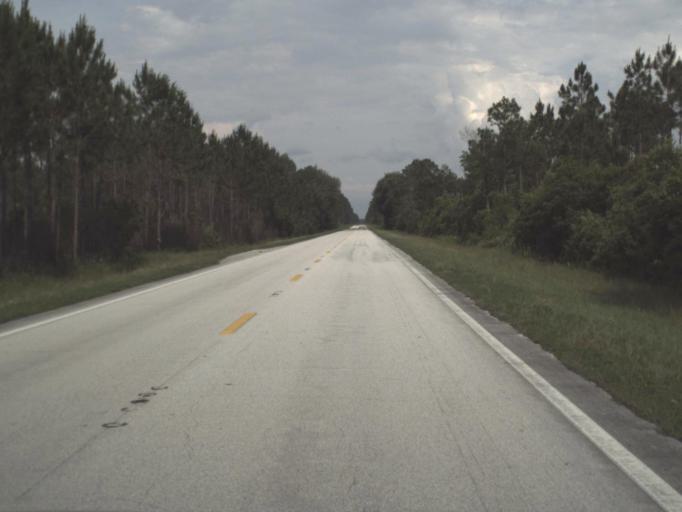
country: US
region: Florida
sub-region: Columbia County
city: Five Points
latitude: 30.5684
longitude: -82.4355
